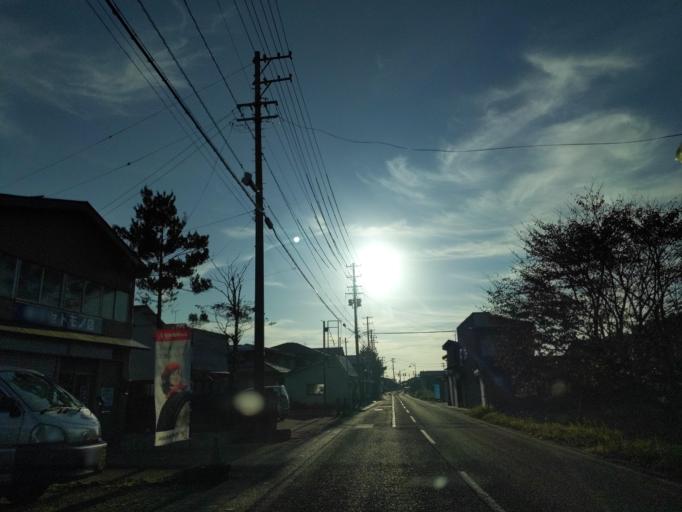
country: JP
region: Niigata
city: Nagaoka
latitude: 37.5796
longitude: 138.7700
